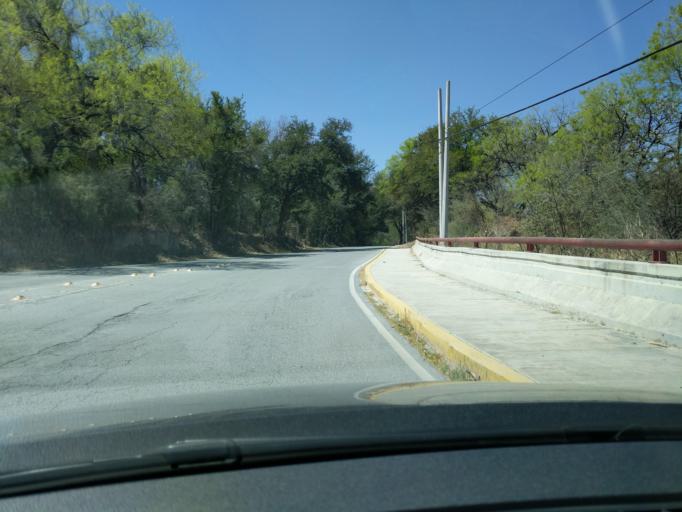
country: MX
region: Nuevo Leon
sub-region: Pesqueria
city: Colinas del Aeropuerto
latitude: 25.8130
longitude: -100.1213
